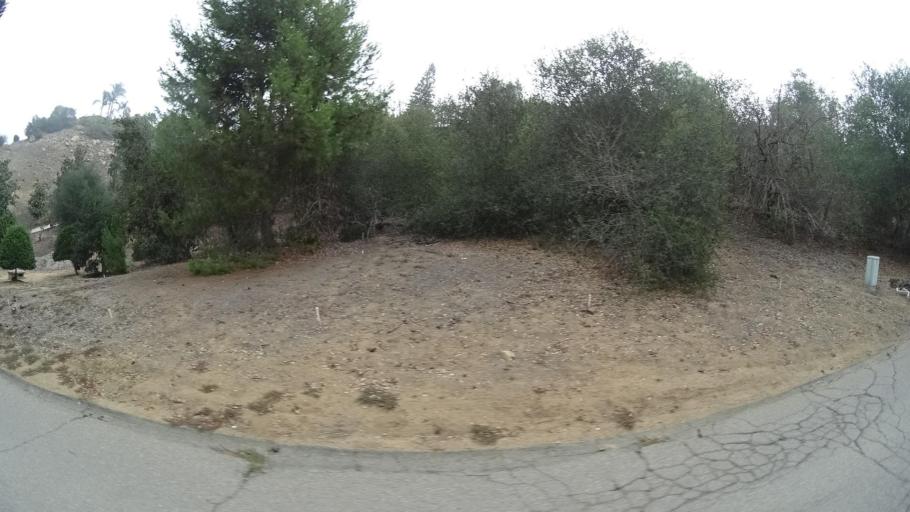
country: US
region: California
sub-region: San Diego County
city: Rainbow
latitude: 33.3530
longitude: -117.1776
